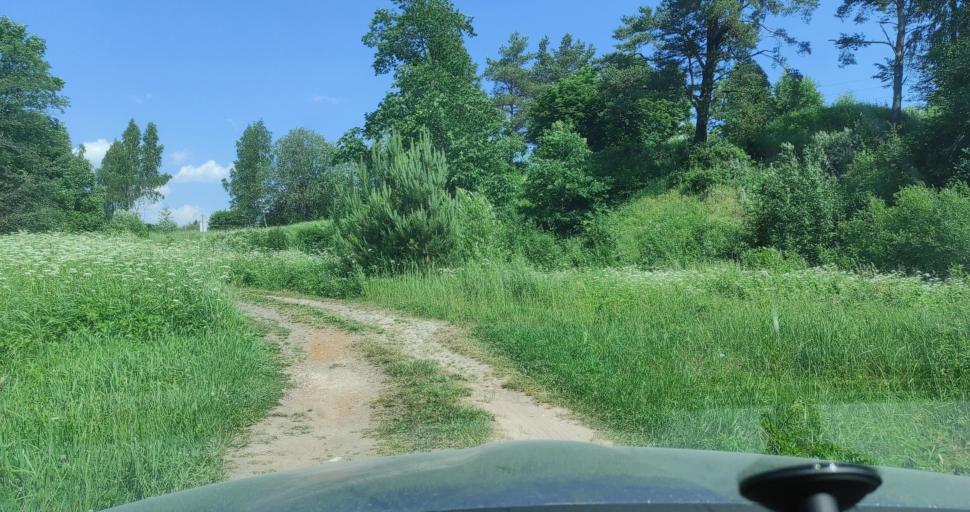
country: LV
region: Aloja
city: Staicele
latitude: 57.8368
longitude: 24.7366
